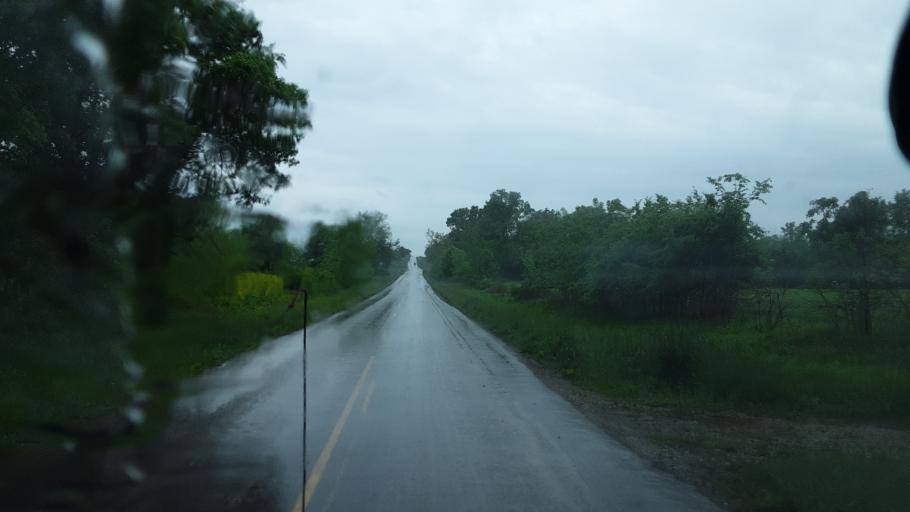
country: US
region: Missouri
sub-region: Randolph County
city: Moberly
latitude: 39.3578
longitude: -92.2683
